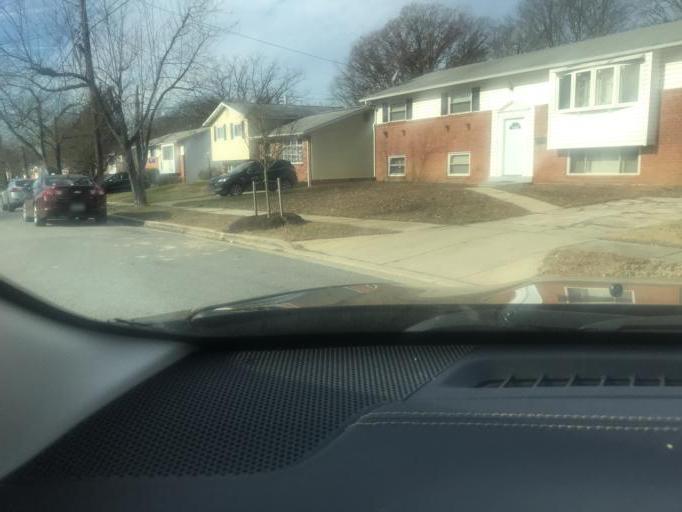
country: US
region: Maryland
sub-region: Prince George's County
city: Oxon Hill
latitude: 38.8108
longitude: -76.9747
